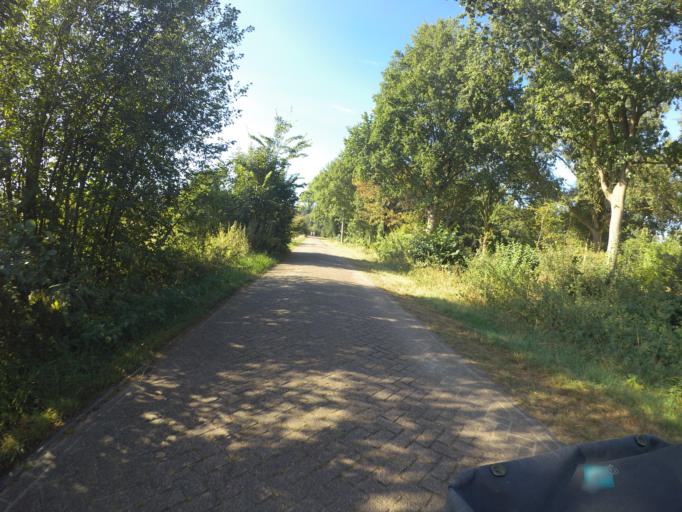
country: NL
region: Overijssel
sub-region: Gemeente Zwolle
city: Zwolle
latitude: 52.5387
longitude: 6.1323
